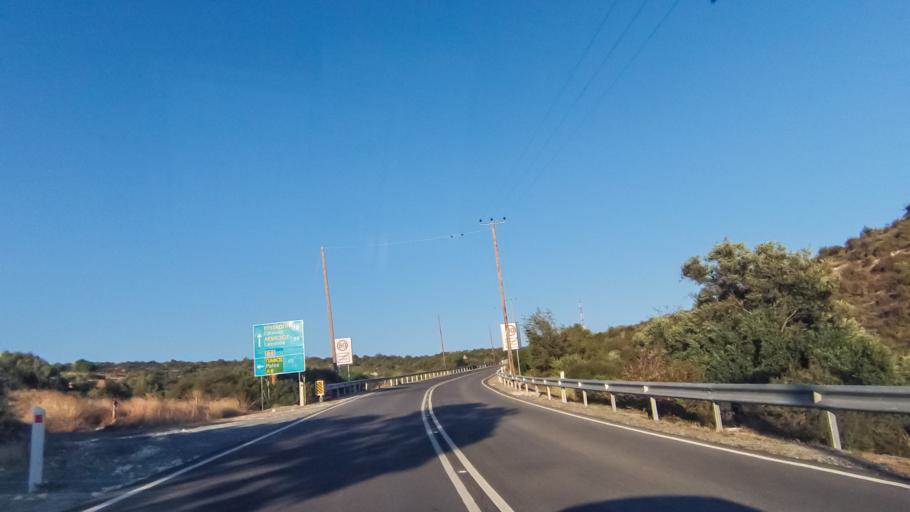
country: CY
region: Limassol
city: Sotira
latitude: 34.6766
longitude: 32.7983
